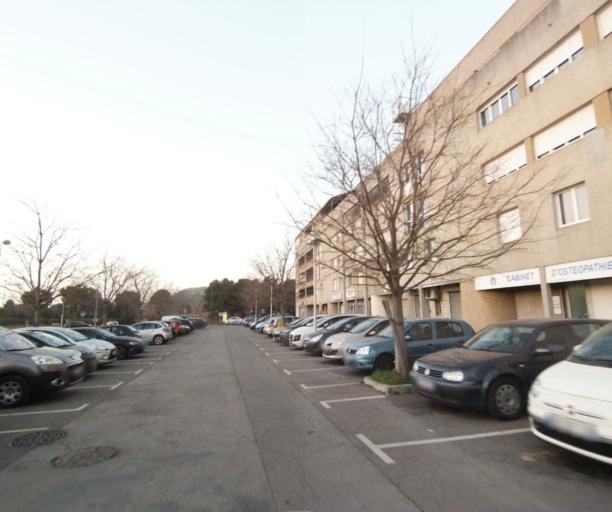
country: FR
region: Provence-Alpes-Cote d'Azur
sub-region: Departement des Bouches-du-Rhone
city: Saint-Victoret
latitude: 43.4266
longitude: 5.2722
